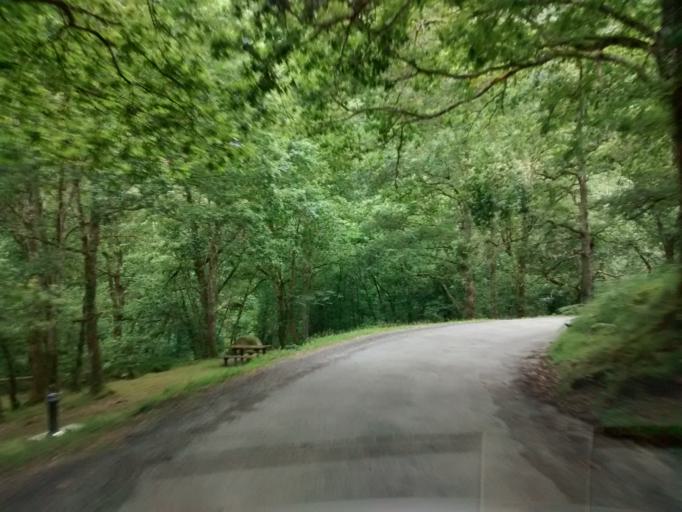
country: ES
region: Asturias
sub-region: Province of Asturias
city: Campo de Caso
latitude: 43.2673
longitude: -5.3377
